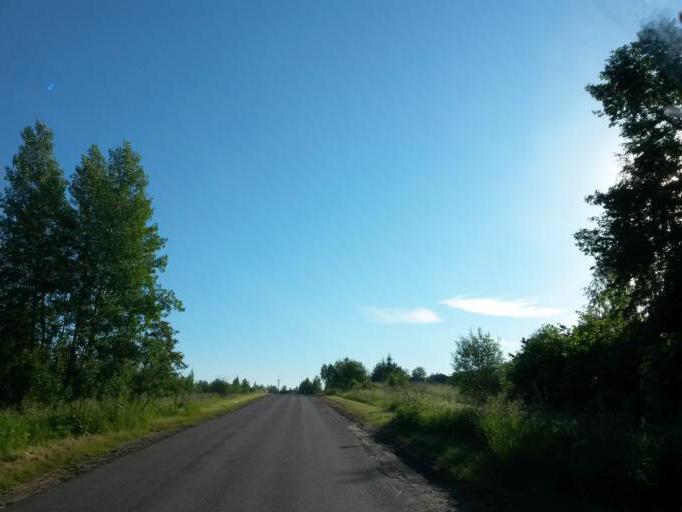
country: RU
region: Moskovskaya
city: Lyubuchany
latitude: 55.2685
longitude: 37.6188
